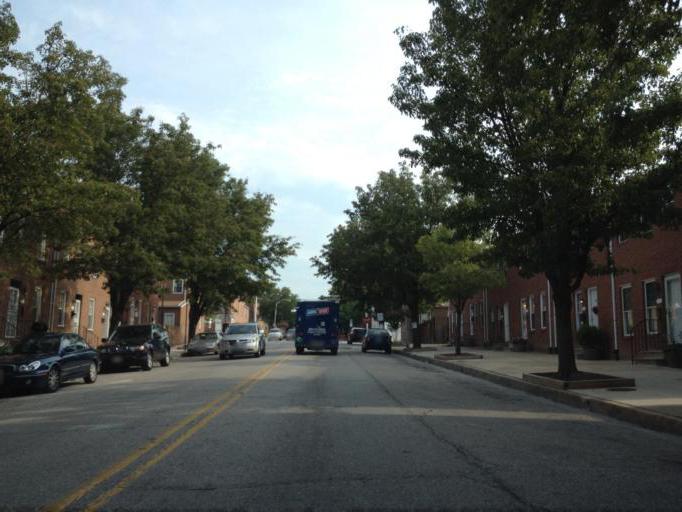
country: US
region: Maryland
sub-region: City of Baltimore
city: Baltimore
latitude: 39.3009
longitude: -76.6002
